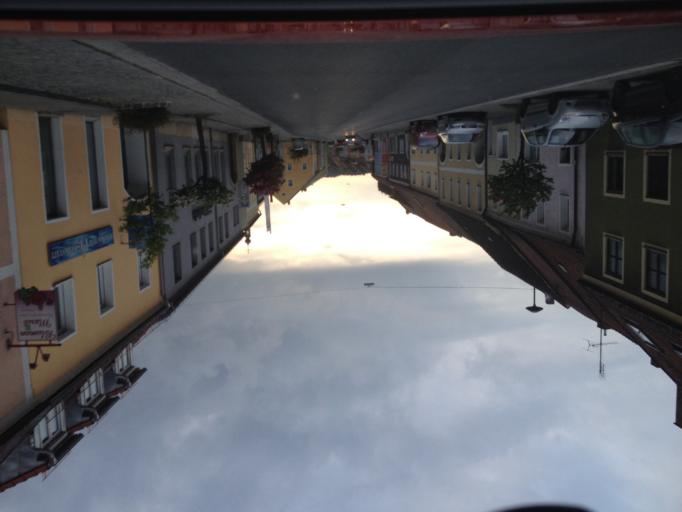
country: DE
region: Bavaria
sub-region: Upper Palatinate
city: Hahnbach
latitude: 49.5349
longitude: 11.8055
